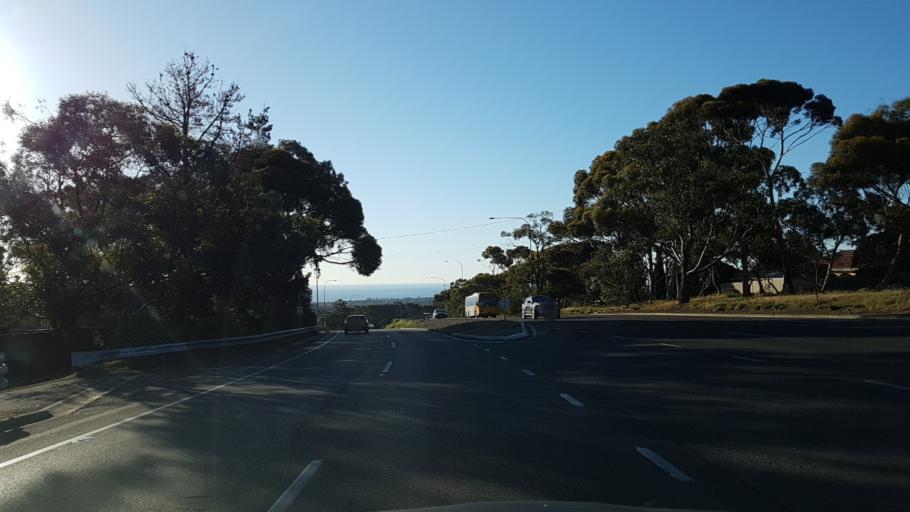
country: AU
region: South Australia
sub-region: Onkaparinga
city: Bedford Park
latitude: -35.0378
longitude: 138.5664
